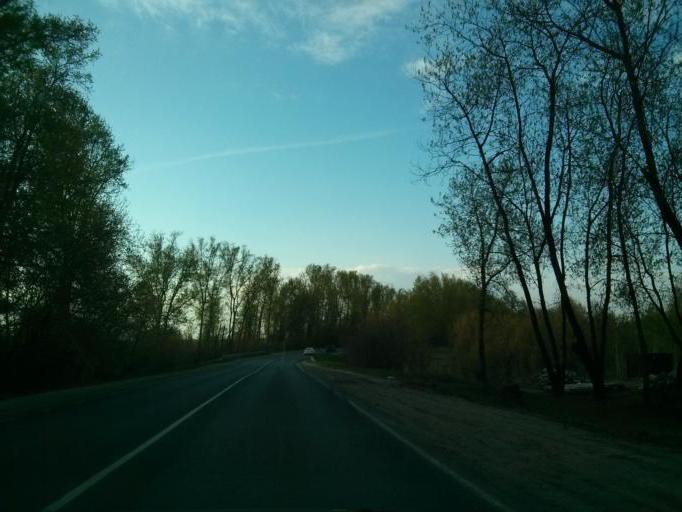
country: RU
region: Vladimir
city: Murom
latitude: 55.6058
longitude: 42.0268
